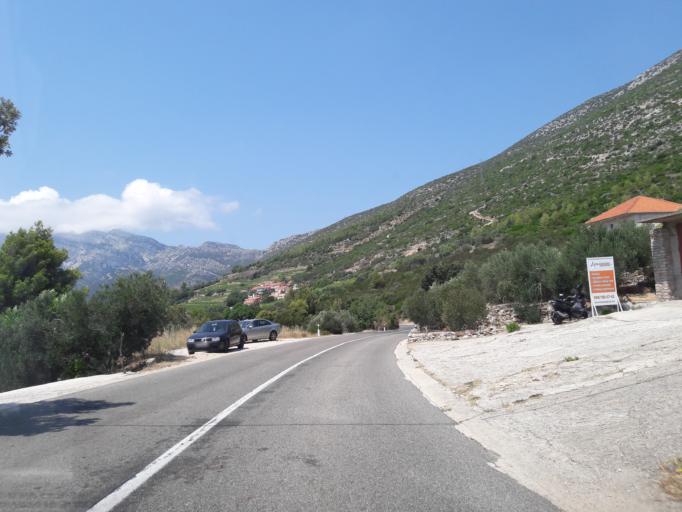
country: HR
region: Dubrovacko-Neretvanska
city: Orebic
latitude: 42.9757
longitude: 17.2306
